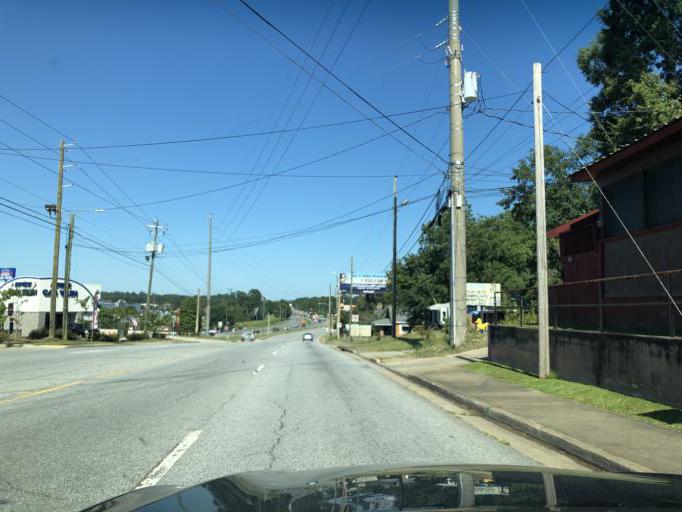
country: US
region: Georgia
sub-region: Muscogee County
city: Columbus
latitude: 32.5048
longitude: -84.9474
